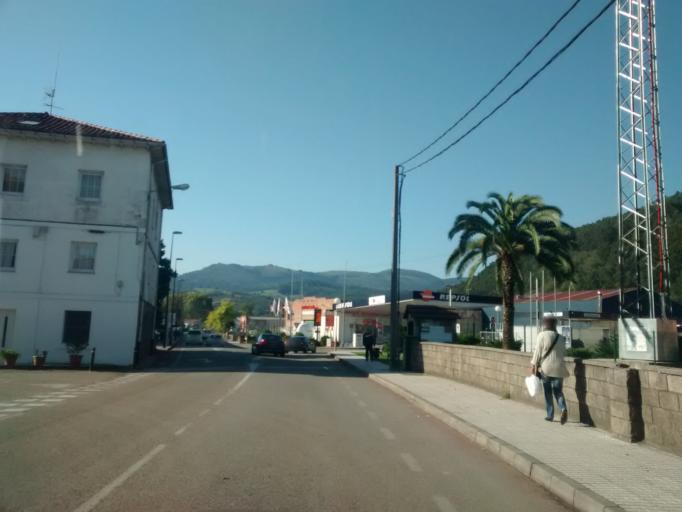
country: ES
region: Cantabria
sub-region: Provincia de Cantabria
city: Cartes
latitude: 43.3334
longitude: -4.0651
